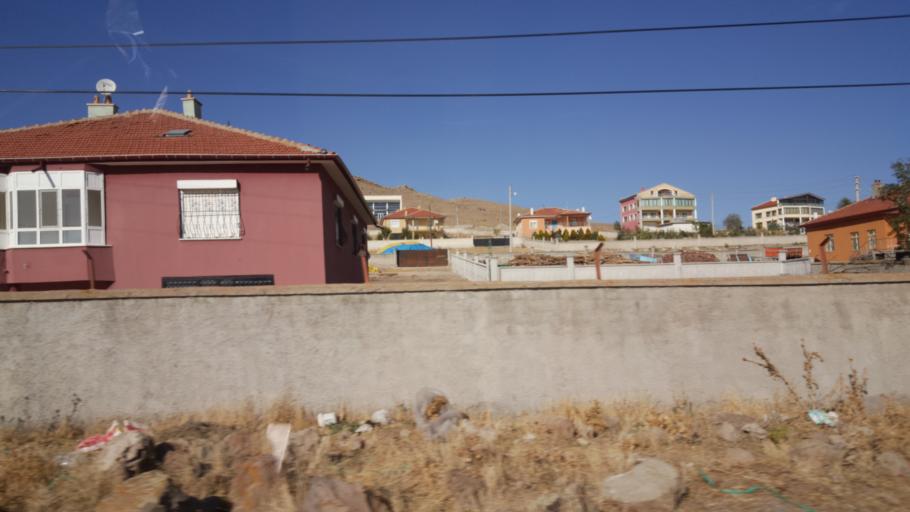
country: TR
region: Ankara
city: Altpinar
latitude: 39.1710
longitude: 32.6903
